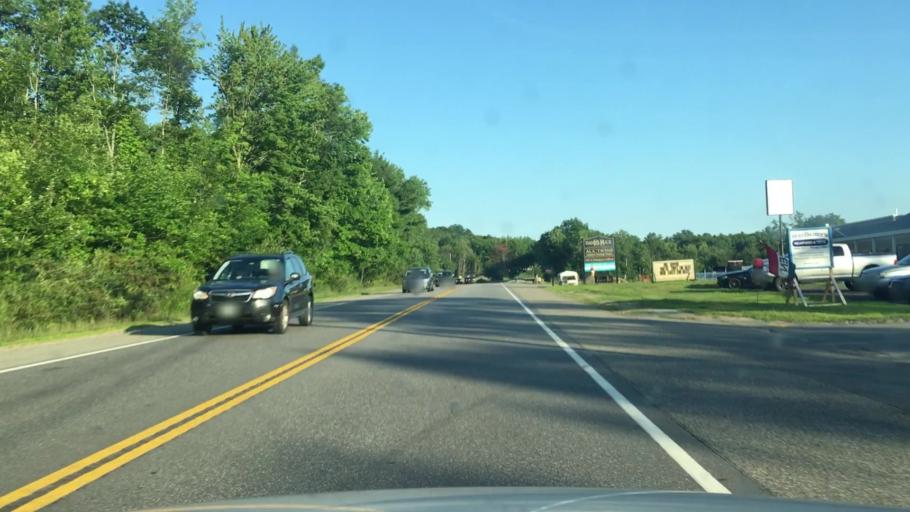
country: US
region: Maine
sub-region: Androscoggin County
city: Lisbon Falls
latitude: 44.0099
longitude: -70.0841
